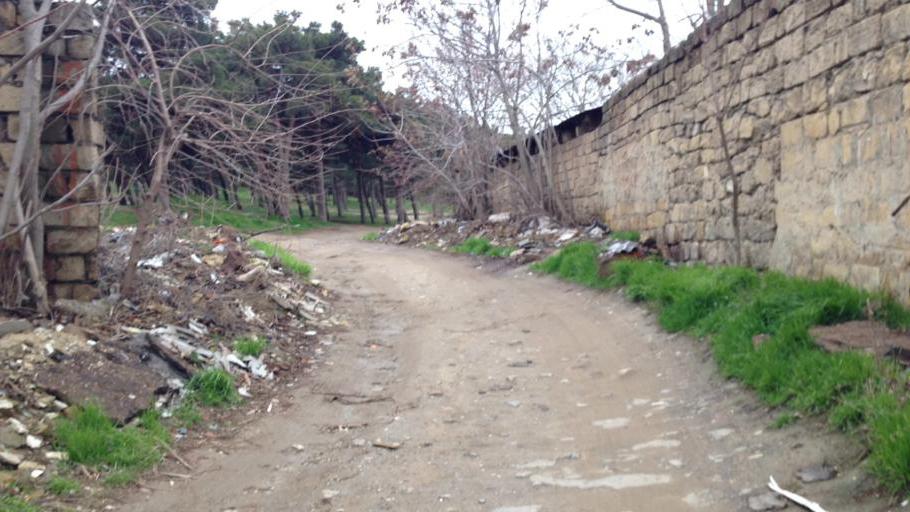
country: AZ
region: Baki
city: Baku
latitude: 40.3933
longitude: 49.8524
